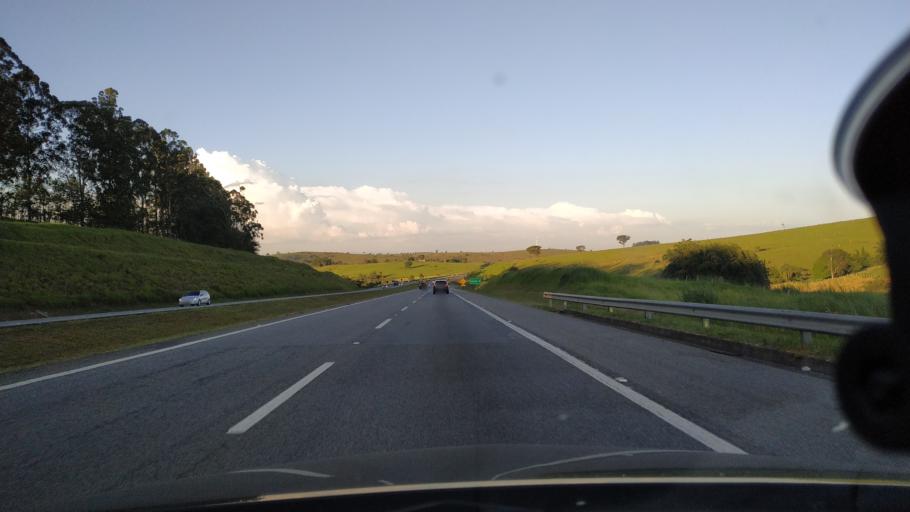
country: BR
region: Sao Paulo
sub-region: Sao Jose Dos Campos
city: Sao Jose dos Campos
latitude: -23.2408
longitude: -45.7876
